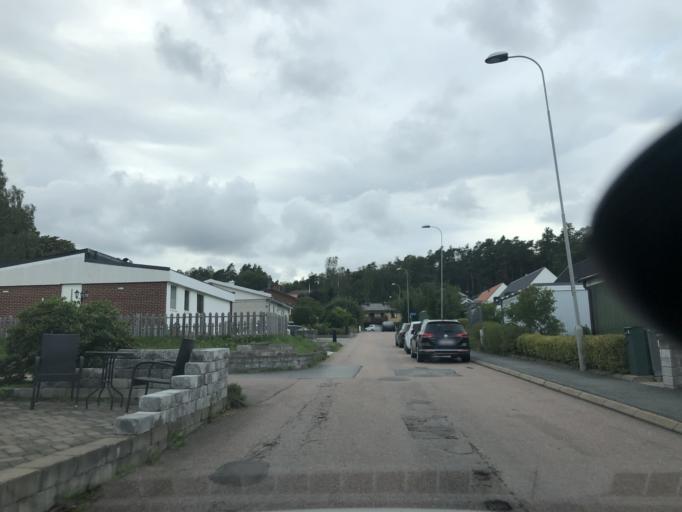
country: SE
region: Vaestra Goetaland
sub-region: Goteborg
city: Goeteborg
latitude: 57.7551
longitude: 11.9604
